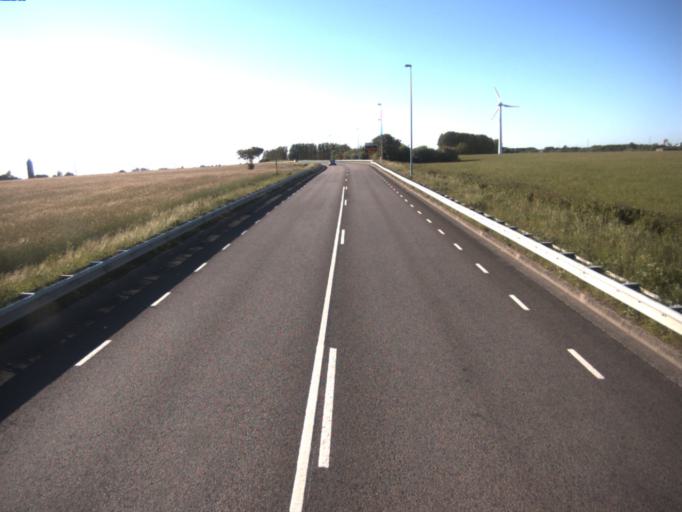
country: SE
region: Skane
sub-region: Helsingborg
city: Rydeback
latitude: 55.9899
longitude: 12.7642
